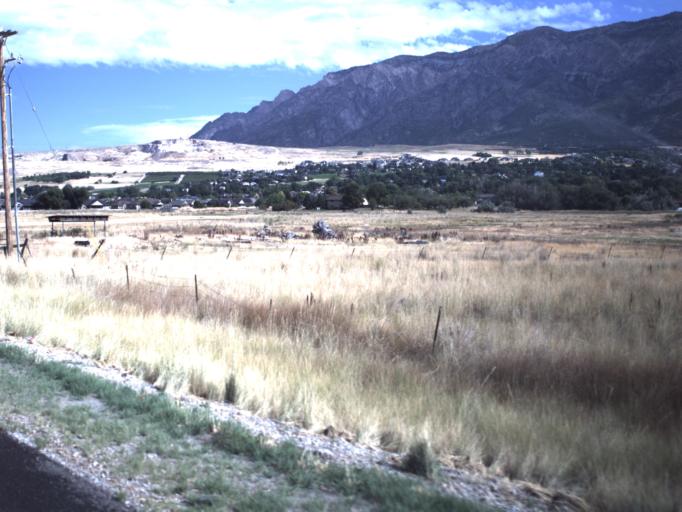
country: US
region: Utah
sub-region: Weber County
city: Pleasant View
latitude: 41.3101
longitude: -112.0082
